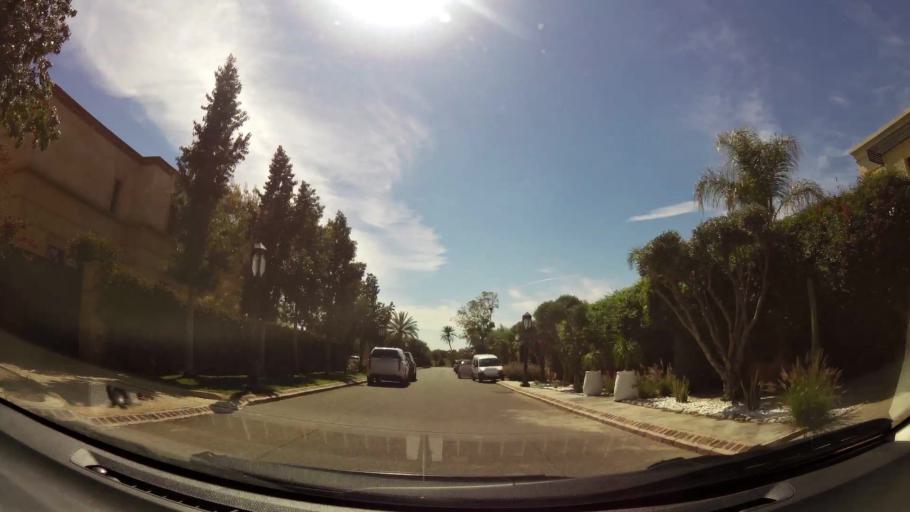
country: MA
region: Marrakech-Tensift-Al Haouz
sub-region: Marrakech
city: Marrakesh
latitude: 31.6177
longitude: -7.9349
